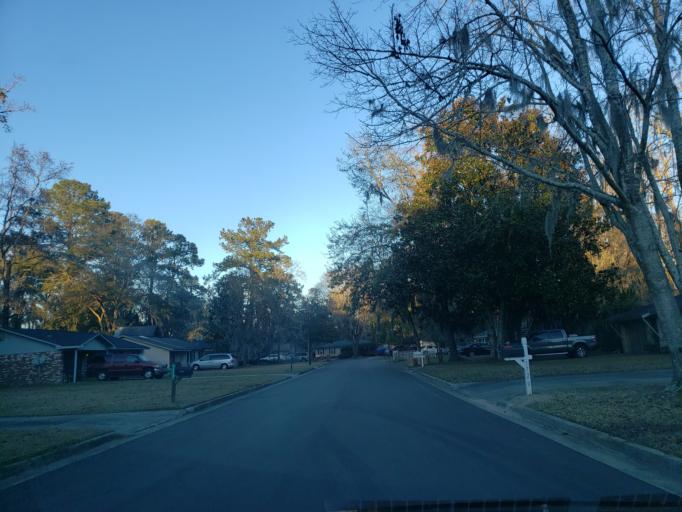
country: US
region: Georgia
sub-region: Chatham County
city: Isle of Hope
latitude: 31.9770
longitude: -81.0981
